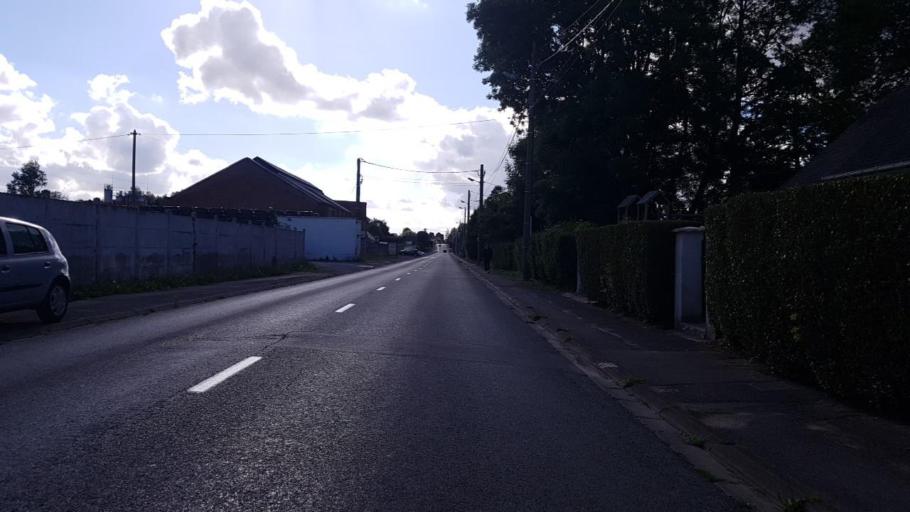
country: FR
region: Picardie
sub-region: Departement de l'Aisne
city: Hirson
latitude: 49.9203
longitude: 4.0749
